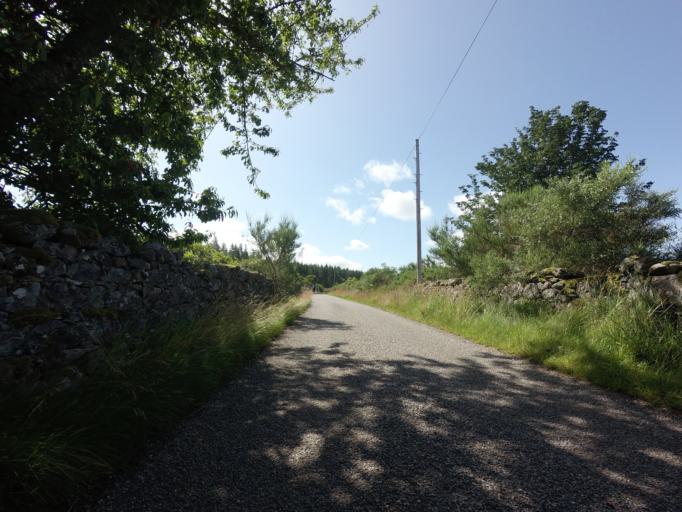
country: GB
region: Scotland
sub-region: Highland
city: Nairn
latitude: 57.5019
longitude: -3.9390
